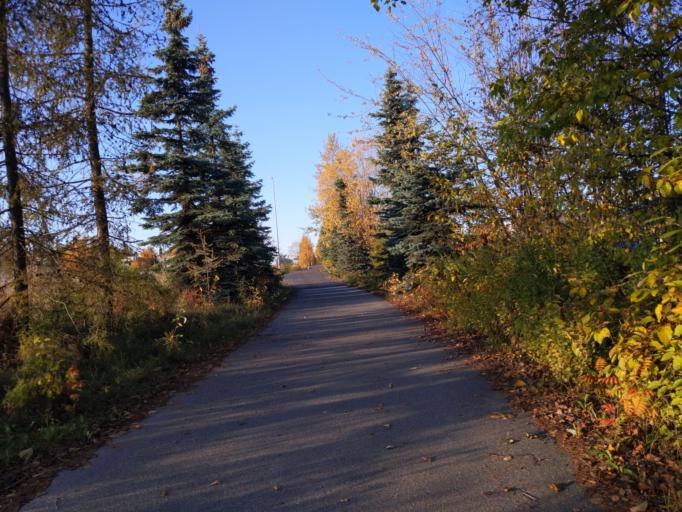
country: US
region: Alaska
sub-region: Anchorage Municipality
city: Anchorage
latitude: 61.1677
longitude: -149.8859
